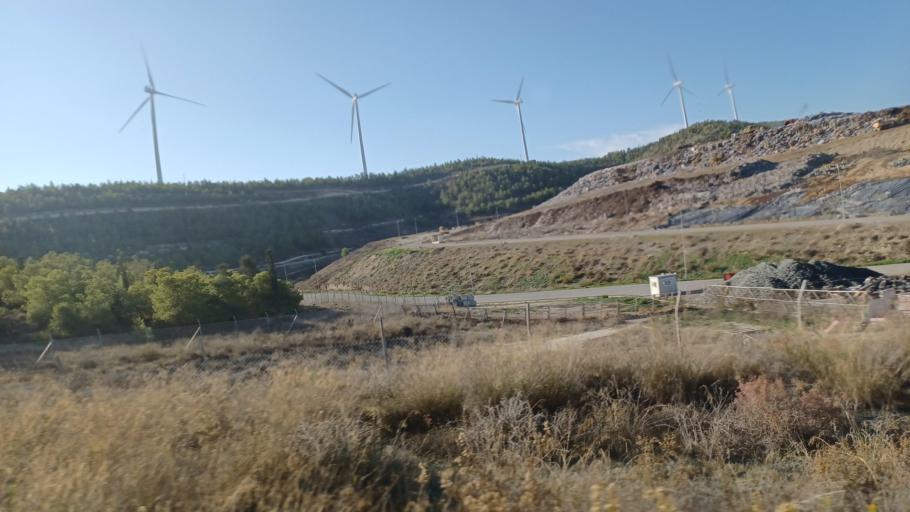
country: CY
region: Larnaka
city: Psevdas
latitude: 34.9630
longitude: 33.5128
